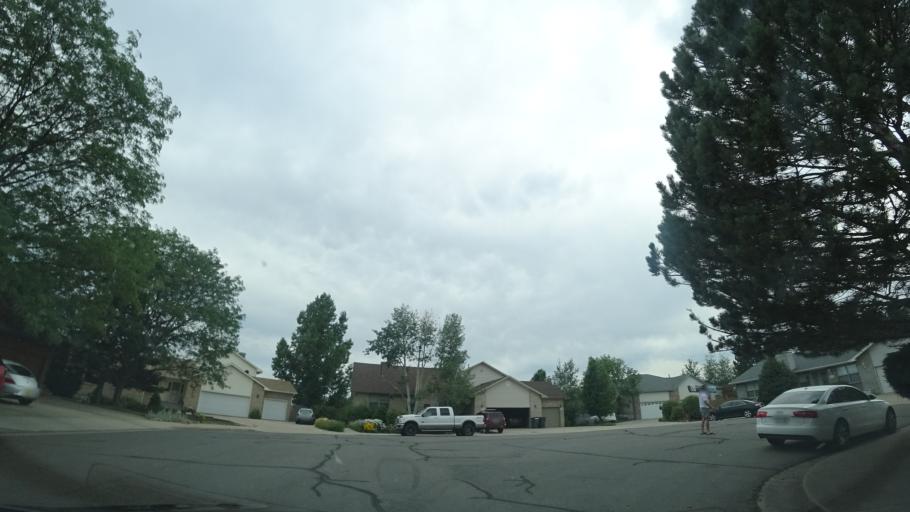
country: US
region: Colorado
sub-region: Jefferson County
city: Lakewood
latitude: 39.7090
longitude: -105.0926
